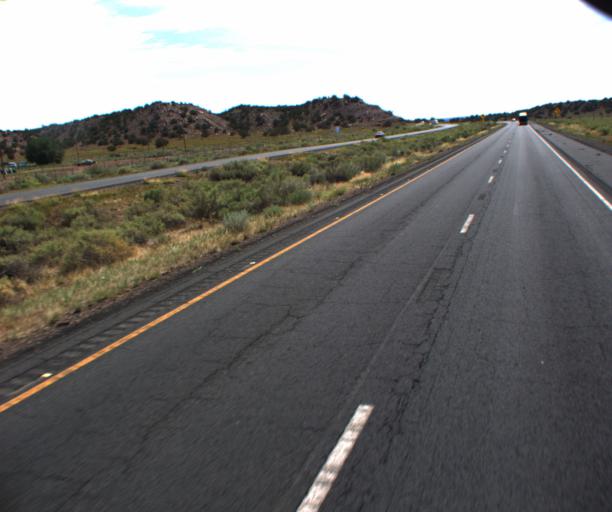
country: US
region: Arizona
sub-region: Apache County
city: Houck
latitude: 35.2803
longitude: -109.1854
